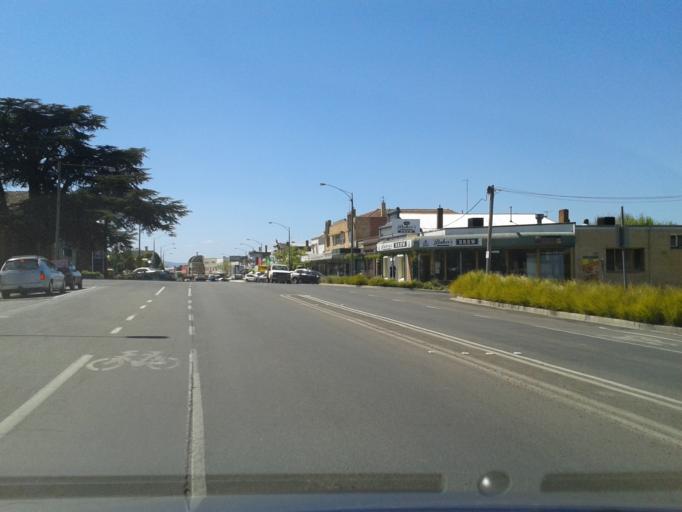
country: AU
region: Victoria
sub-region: Ararat
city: Ararat
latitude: -37.2846
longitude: 142.9264
